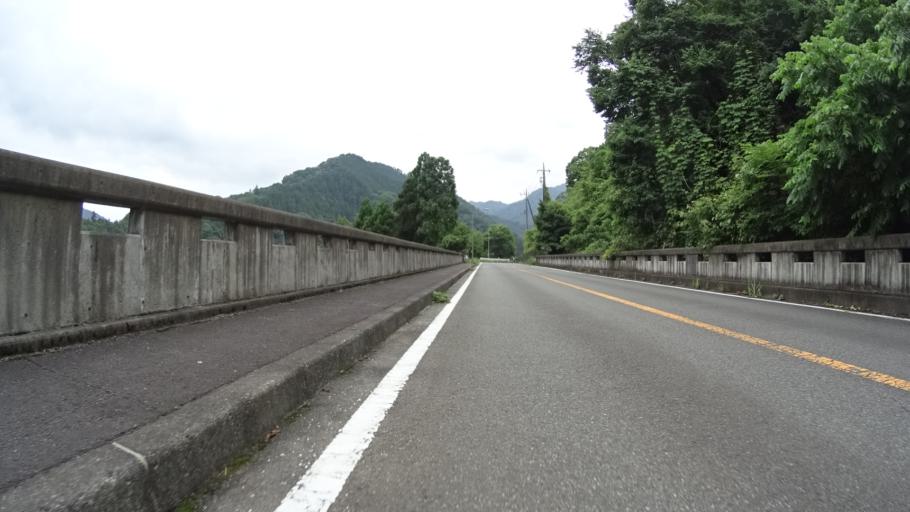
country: JP
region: Kanagawa
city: Hadano
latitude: 35.5163
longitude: 139.2327
